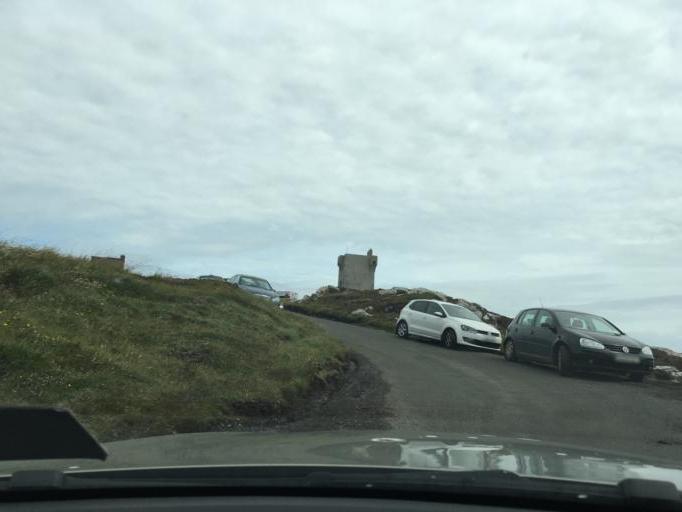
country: IE
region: Ulster
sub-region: County Donegal
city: Carndonagh
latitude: 55.3805
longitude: -7.3751
